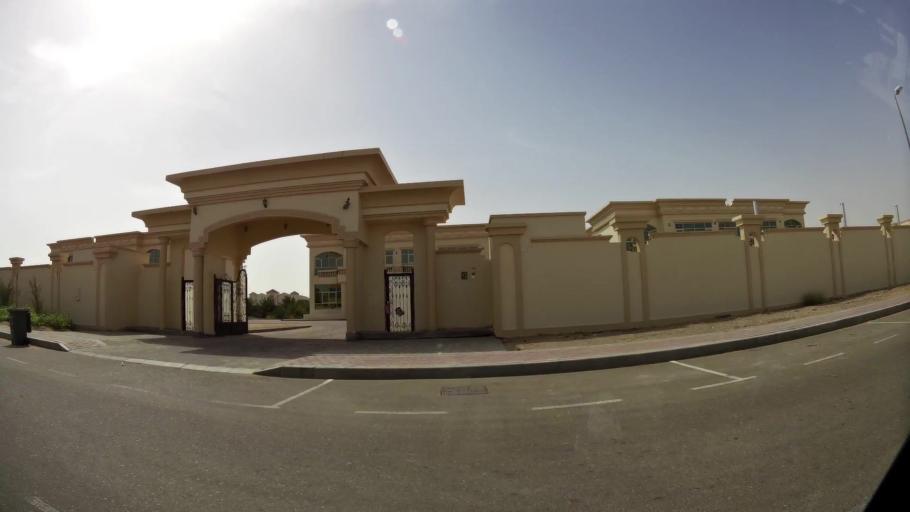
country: AE
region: Abu Dhabi
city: Al Ain
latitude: 24.1712
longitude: 55.6943
